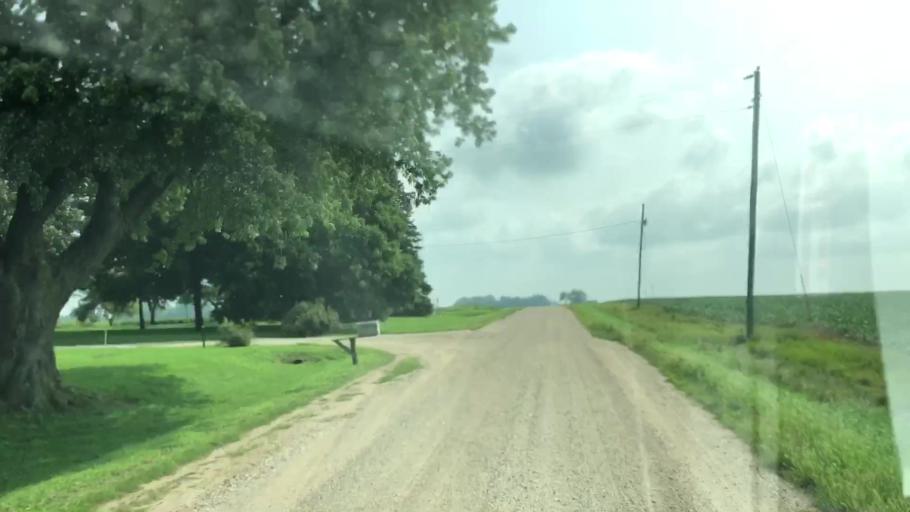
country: US
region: Iowa
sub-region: O'Brien County
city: Sheldon
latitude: 43.2005
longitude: -95.9161
